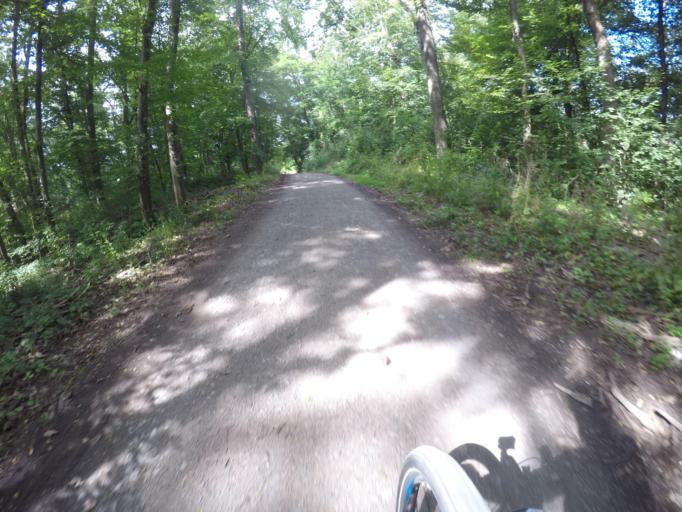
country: DE
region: Baden-Wuerttemberg
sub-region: Karlsruhe Region
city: Otisheim
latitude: 48.9798
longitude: 8.7877
